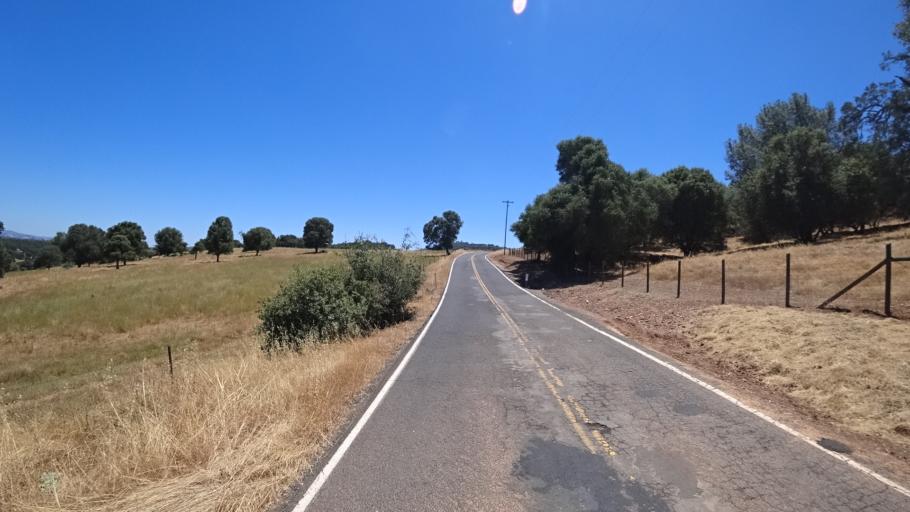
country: US
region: California
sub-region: Calaveras County
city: San Andreas
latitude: 38.0972
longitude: -120.6597
